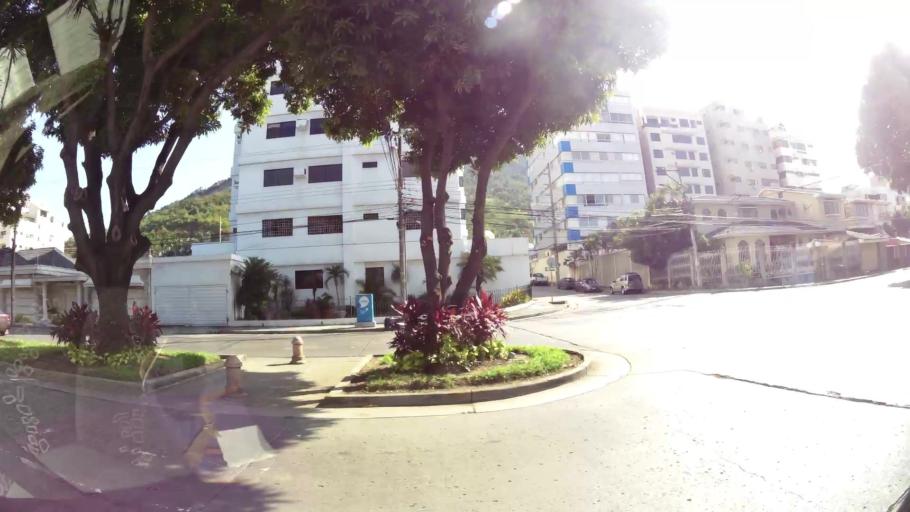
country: EC
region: Guayas
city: Guayaquil
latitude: -2.1687
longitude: -79.9442
